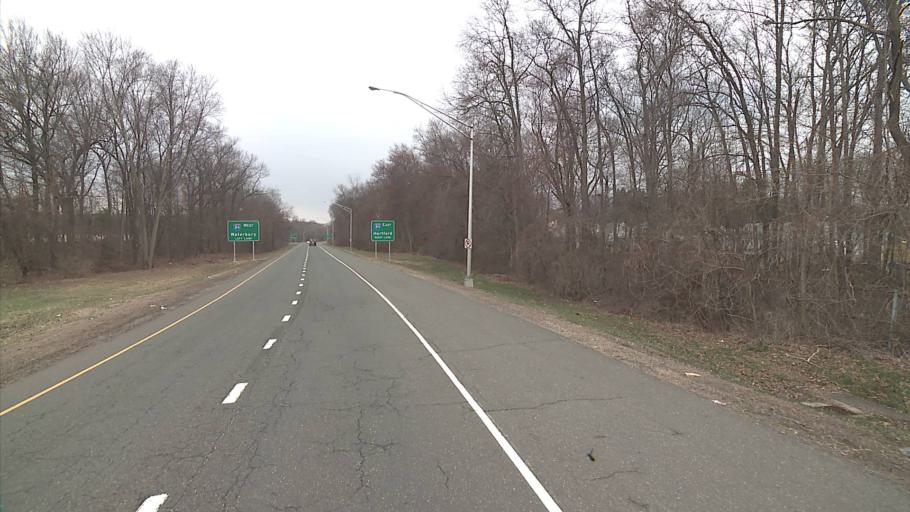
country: US
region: Connecticut
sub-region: Hartford County
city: New Britain
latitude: 41.6779
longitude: -72.8118
